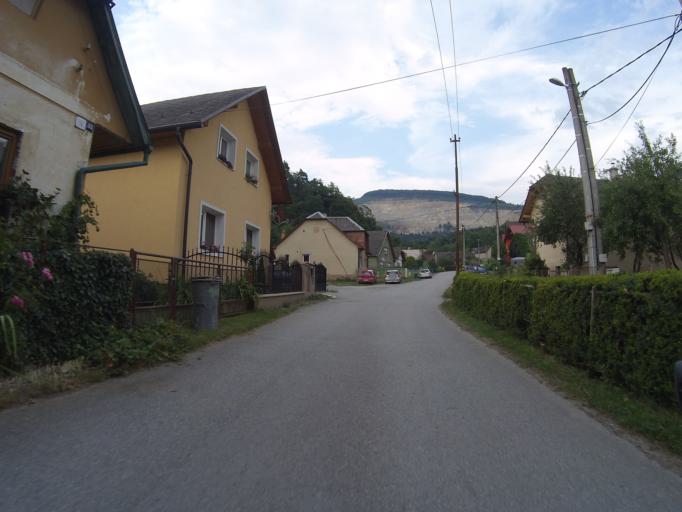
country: SK
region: Nitriansky
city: Puchov
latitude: 49.0380
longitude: 18.3156
